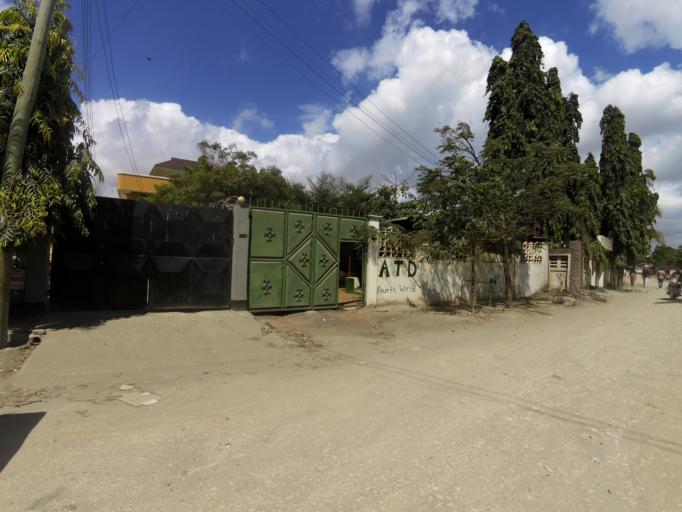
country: TZ
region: Dar es Salaam
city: Magomeni
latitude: -6.7889
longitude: 39.2561
